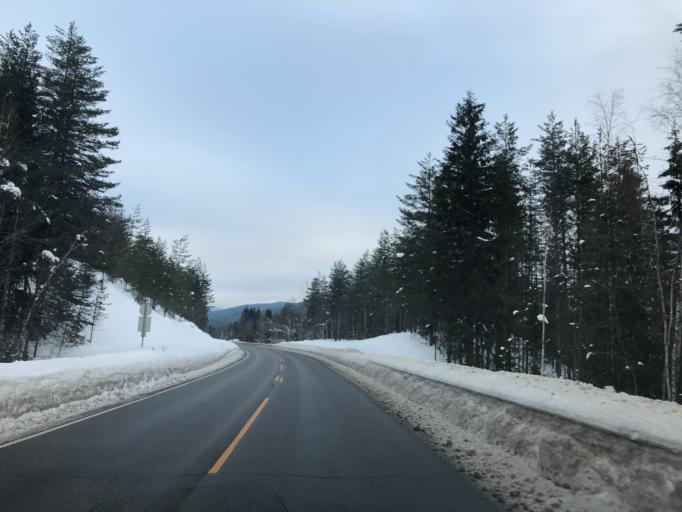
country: NO
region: Hedmark
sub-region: Trysil
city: Innbygda
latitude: 61.2634
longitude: 12.3083
